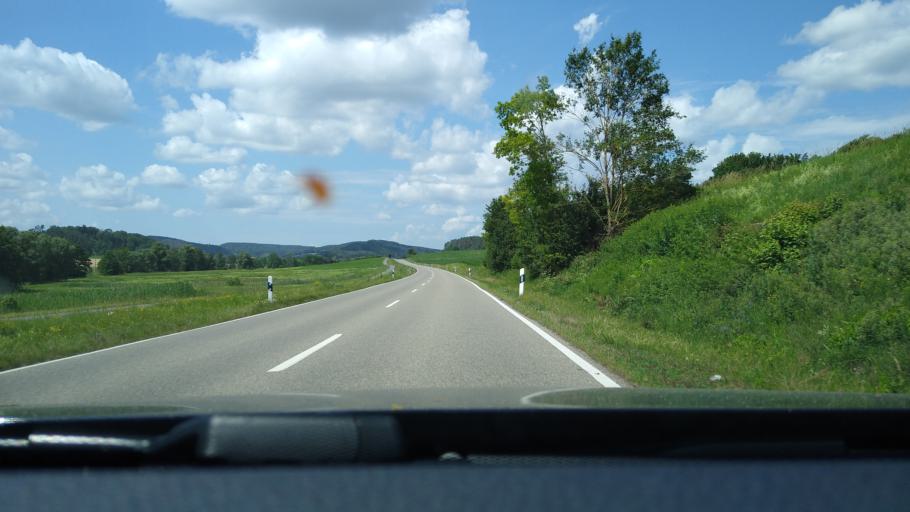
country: DE
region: Bavaria
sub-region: Regierungsbezirk Mittelfranken
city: Neuhof an der Zenn
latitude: 49.4573
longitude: 10.6293
